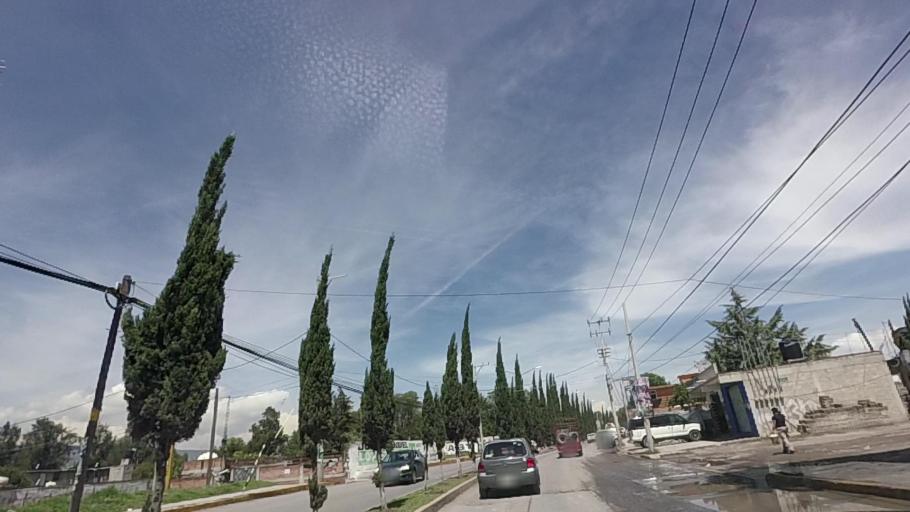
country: MX
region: Mexico
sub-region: Huehuetoca
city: Casa Nueva
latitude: 19.8306
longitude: -99.2198
